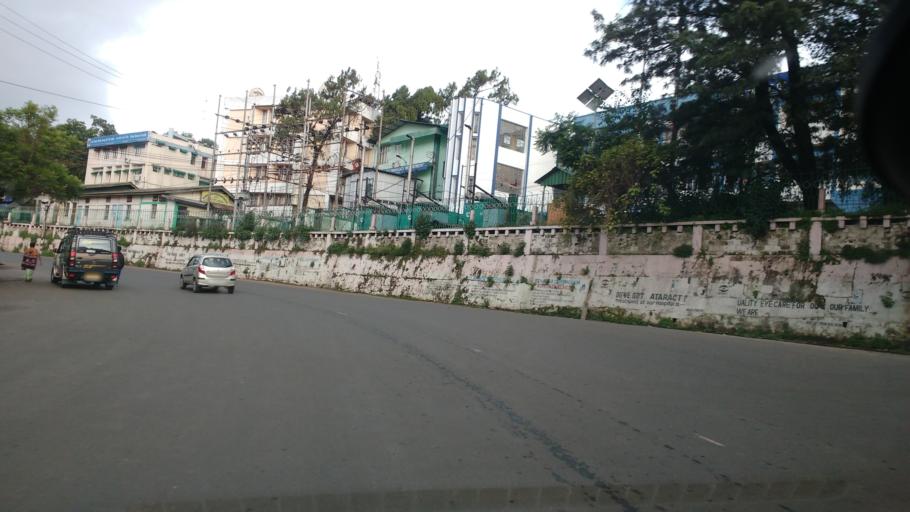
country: IN
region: Meghalaya
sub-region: East Khasi Hills
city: Shillong
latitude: 25.5709
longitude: 91.8857
